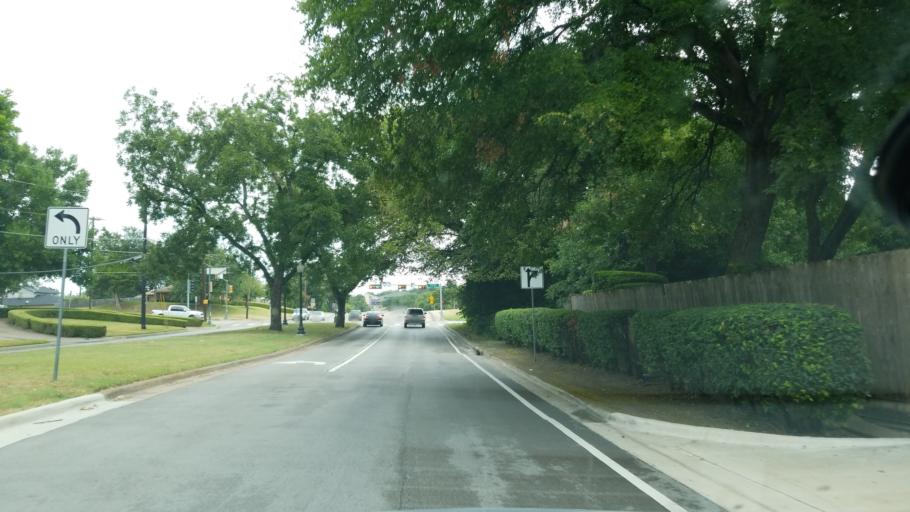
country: US
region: Texas
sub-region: Dallas County
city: Duncanville
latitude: 32.6727
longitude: -96.8410
